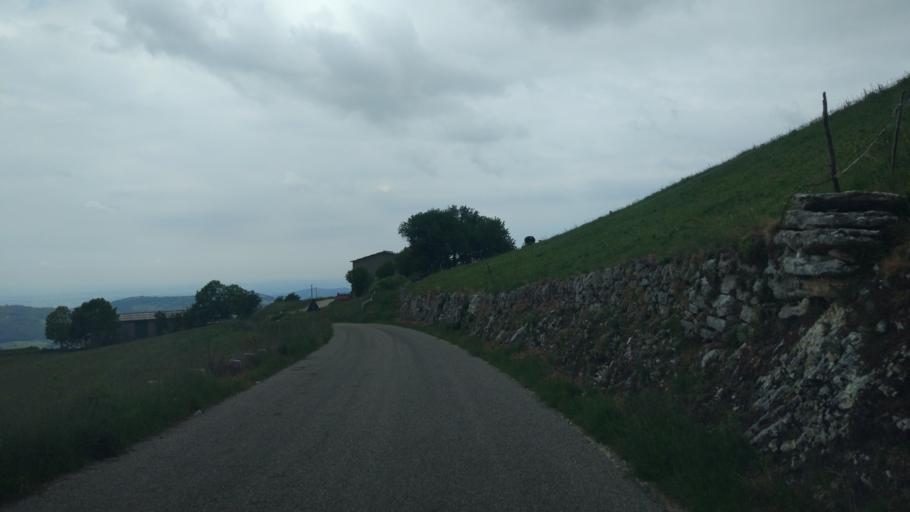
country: IT
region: Veneto
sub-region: Provincia di Verona
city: Erbezzo
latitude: 45.6528
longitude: 10.9997
